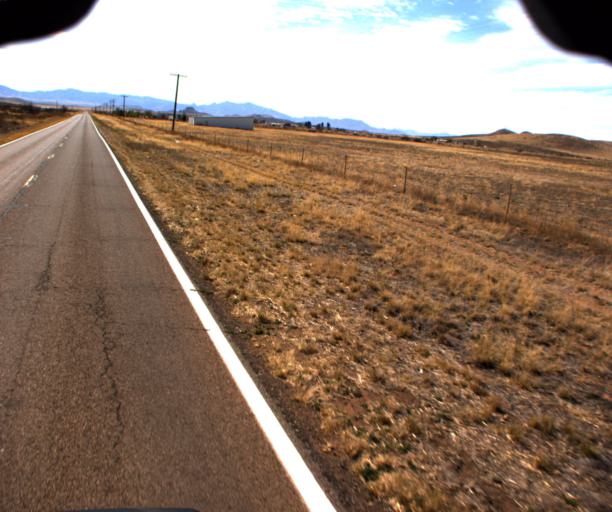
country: US
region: Arizona
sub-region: Cochise County
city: Willcox
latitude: 31.8837
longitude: -109.6742
